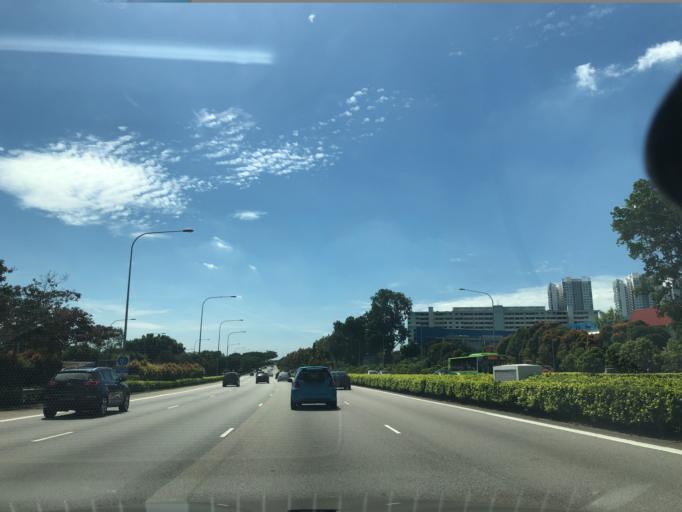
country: SG
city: Singapore
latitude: 1.3750
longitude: 103.8588
